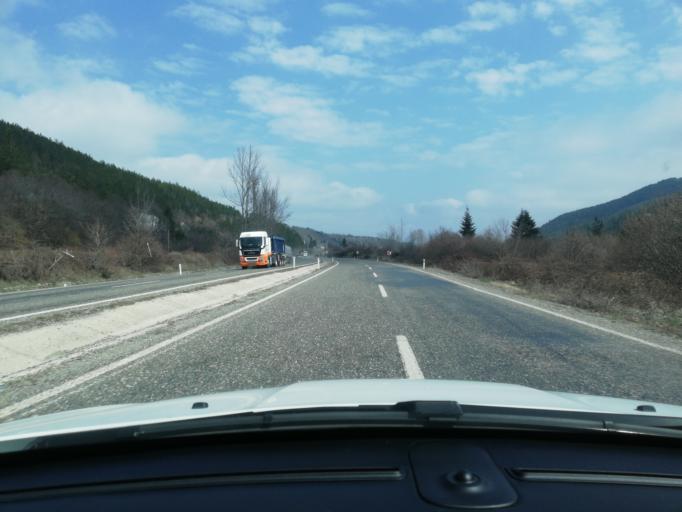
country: TR
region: Kastamonu
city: Kuzyaka
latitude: 41.1960
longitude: 33.7961
